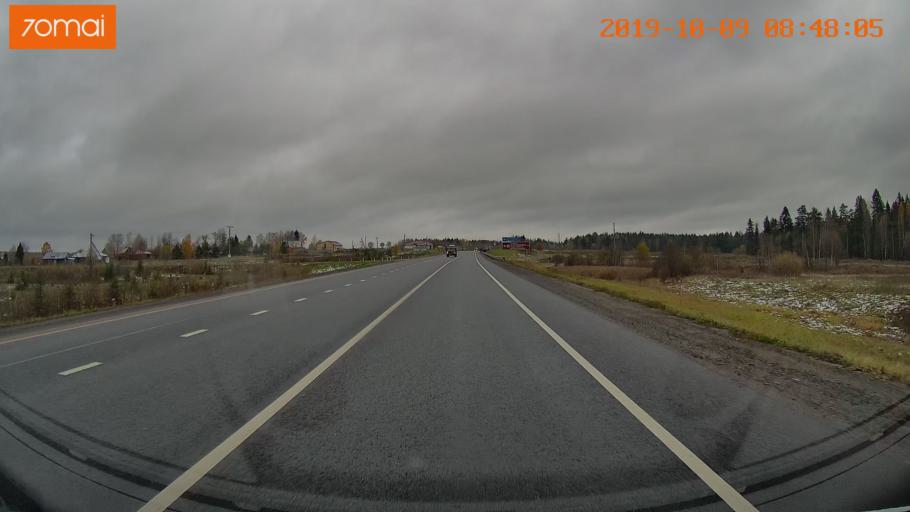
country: RU
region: Vologda
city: Vologda
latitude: 59.0707
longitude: 40.0319
